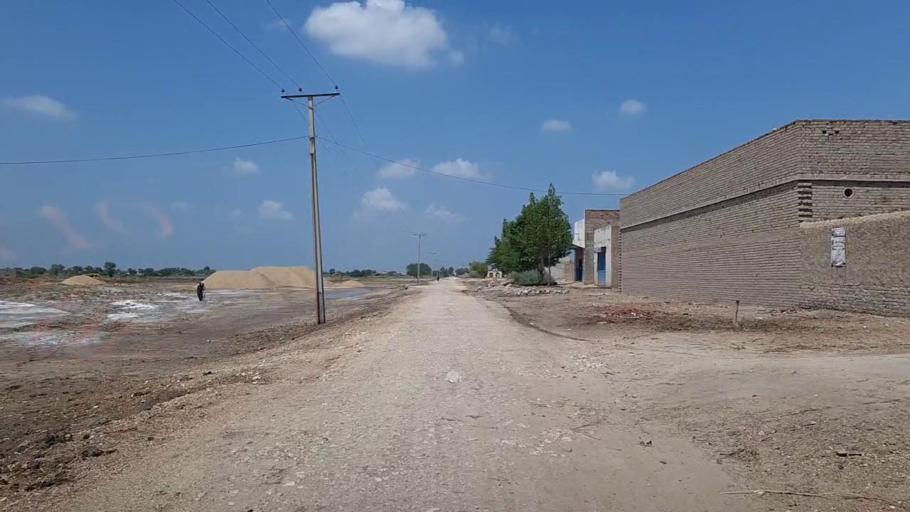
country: PK
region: Sindh
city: Kandiaro
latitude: 27.0034
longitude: 68.2579
